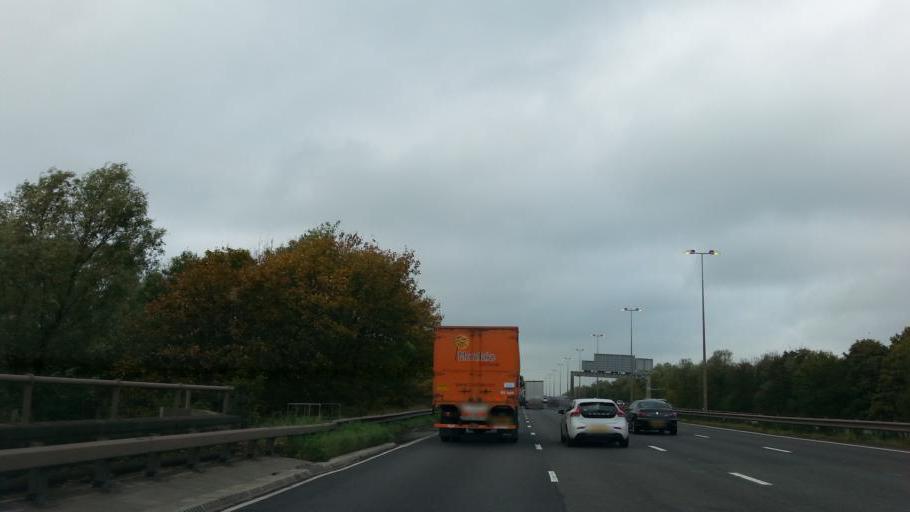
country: GB
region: England
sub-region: Staffordshire
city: Featherstone
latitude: 52.6752
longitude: -2.0847
